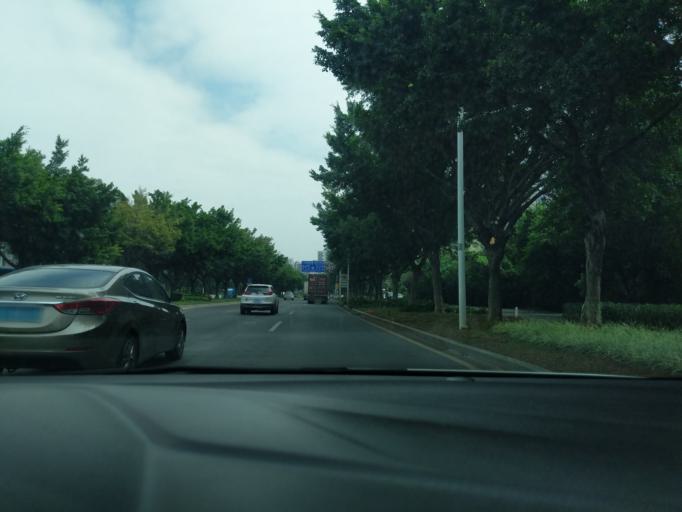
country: CN
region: Guangdong
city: Nansha
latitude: 22.7535
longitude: 113.5760
